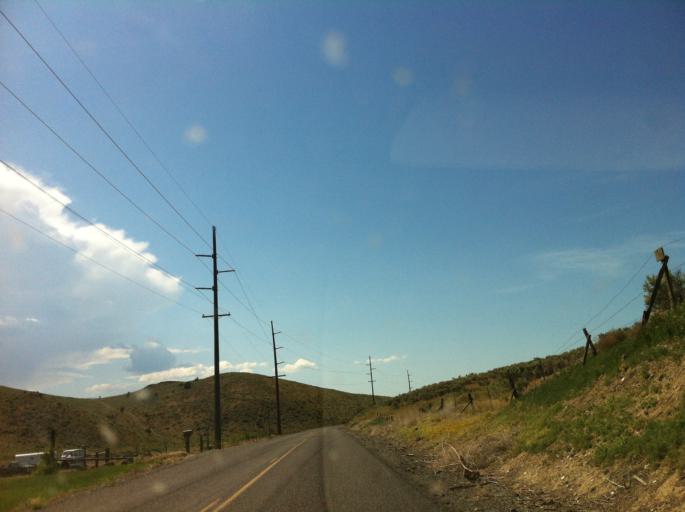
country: US
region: Oregon
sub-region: Baker County
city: Baker City
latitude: 44.7190
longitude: -117.7740
